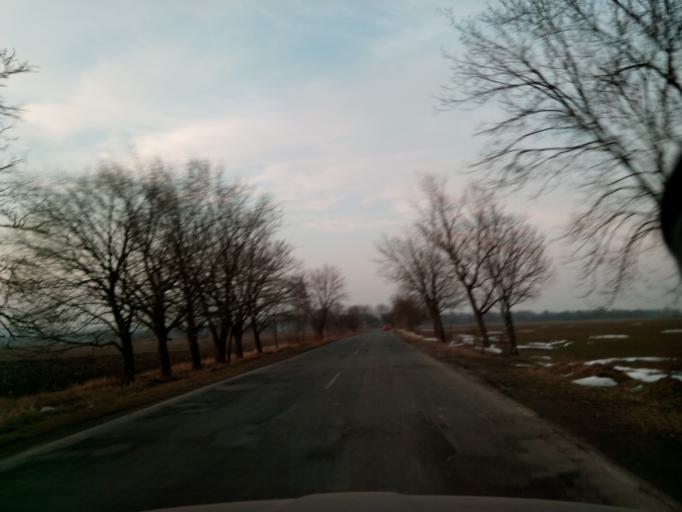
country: HU
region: Borsod-Abauj-Zemplen
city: Gonc
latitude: 48.4867
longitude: 21.2524
